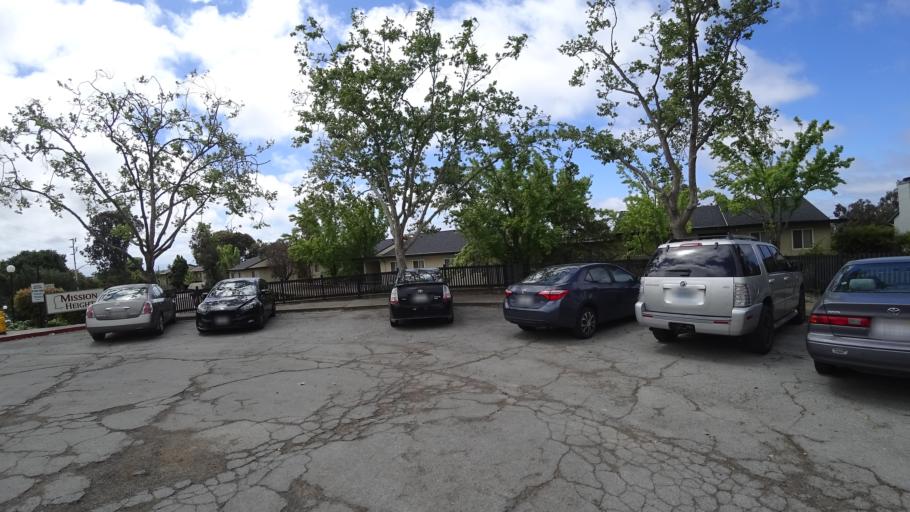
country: US
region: California
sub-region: Alameda County
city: Hayward
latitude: 37.6387
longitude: -122.0538
